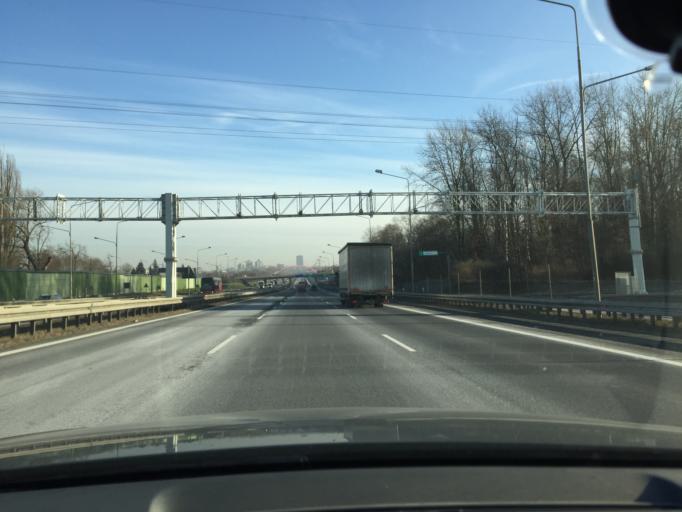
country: PL
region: Silesian Voivodeship
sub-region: Katowice
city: Katowice
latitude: 50.2542
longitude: 18.9771
